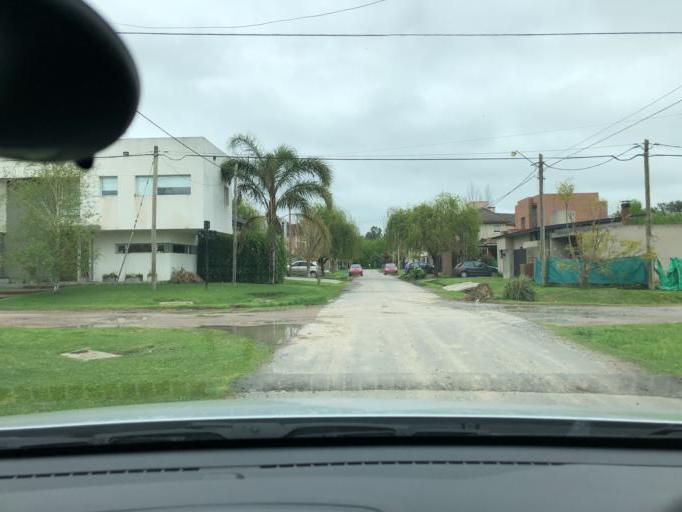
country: AR
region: Buenos Aires
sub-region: Partido de La Plata
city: La Plata
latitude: -34.8597
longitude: -58.0501
